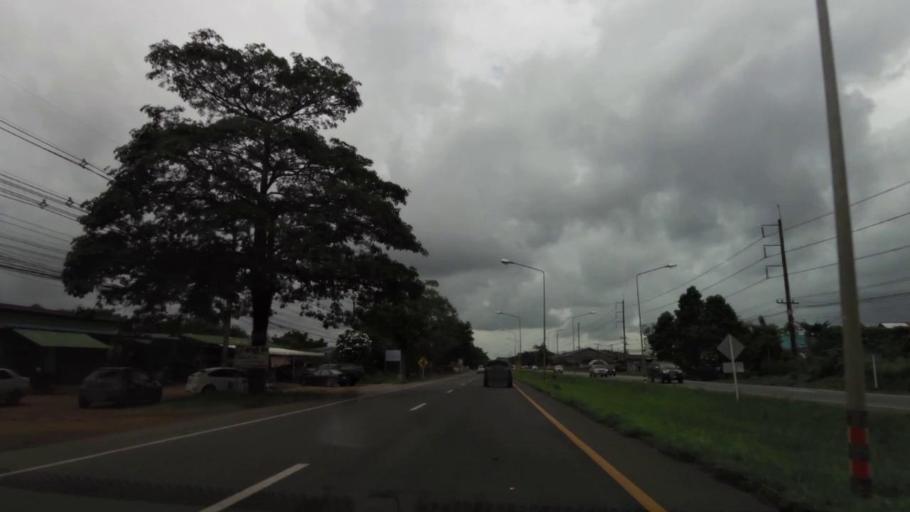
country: TH
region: Chanthaburi
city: Tha Mai
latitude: 12.6554
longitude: 102.0110
